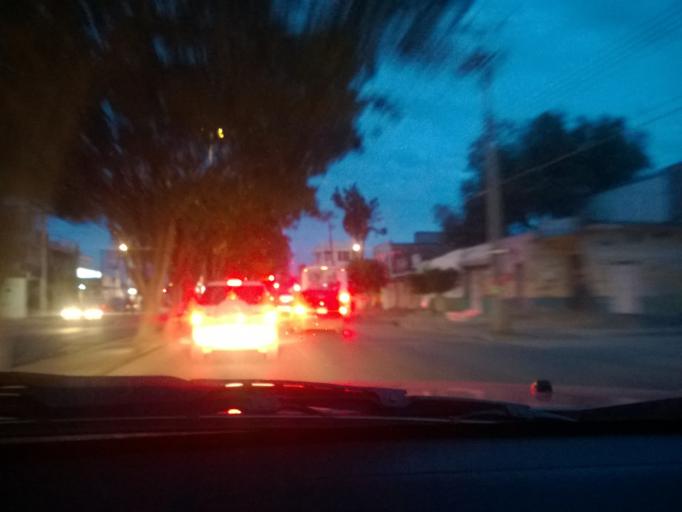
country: MX
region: Guanajuato
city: Leon
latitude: 21.1298
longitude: -101.6528
